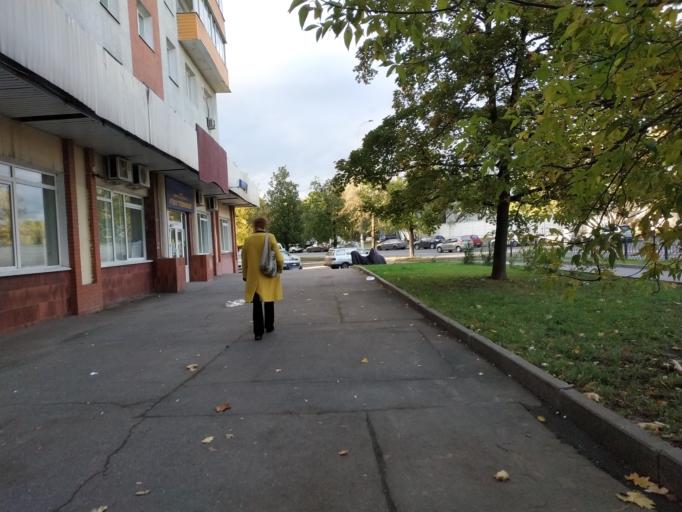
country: RU
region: Moscow
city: Khimki
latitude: 55.8644
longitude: 37.4333
